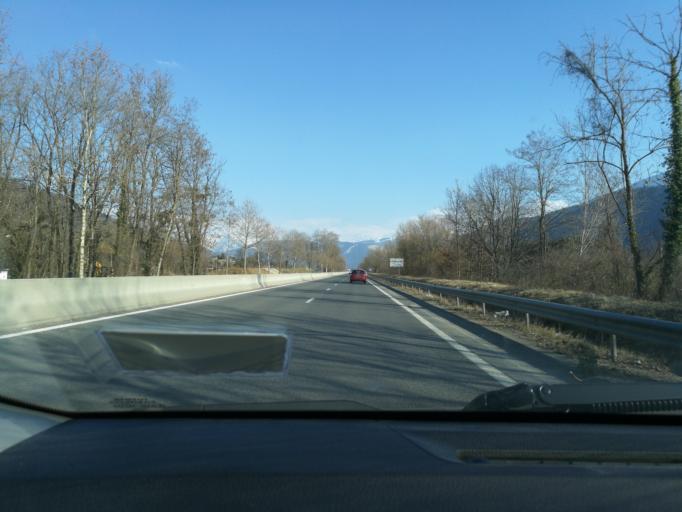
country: FR
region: Rhone-Alpes
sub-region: Departement de la Haute-Savoie
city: Ayse
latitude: 46.0759
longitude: 6.4352
